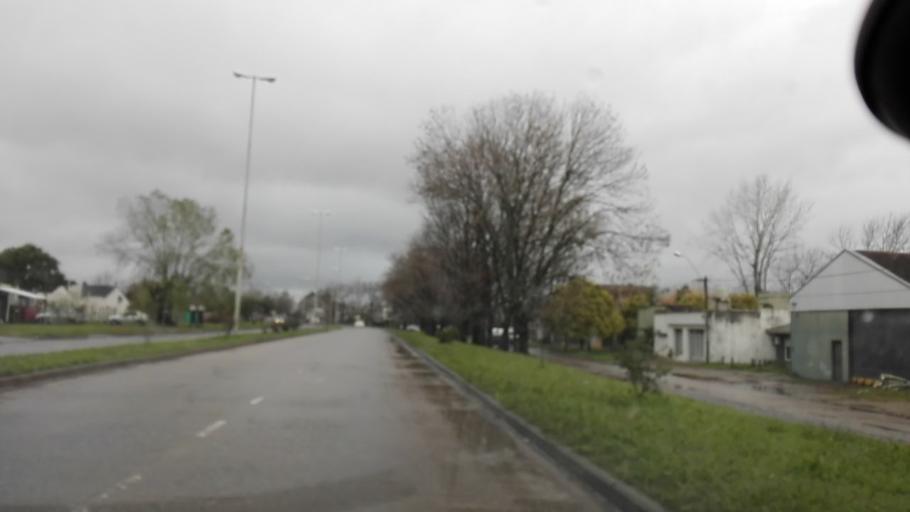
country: AR
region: Buenos Aires
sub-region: Partido de Brandsen
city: Brandsen
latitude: -35.1752
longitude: -58.2374
